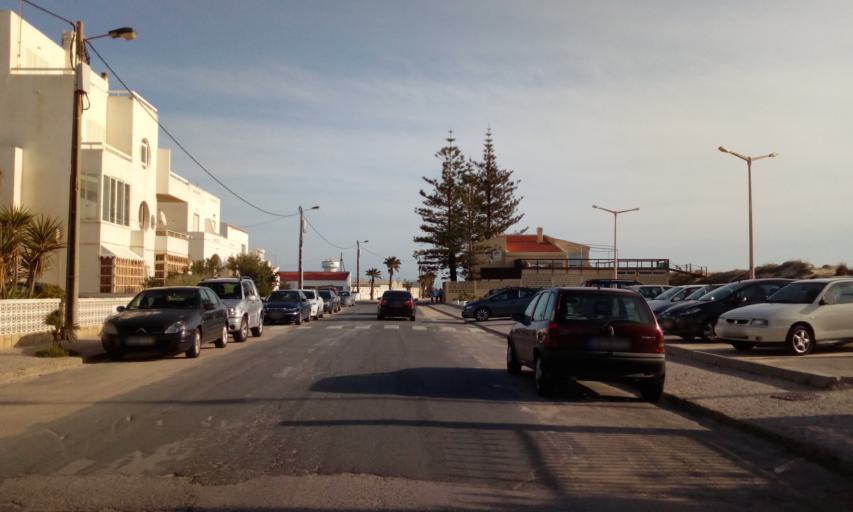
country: PT
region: Faro
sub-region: Faro
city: Faro
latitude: 37.0071
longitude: -7.9932
